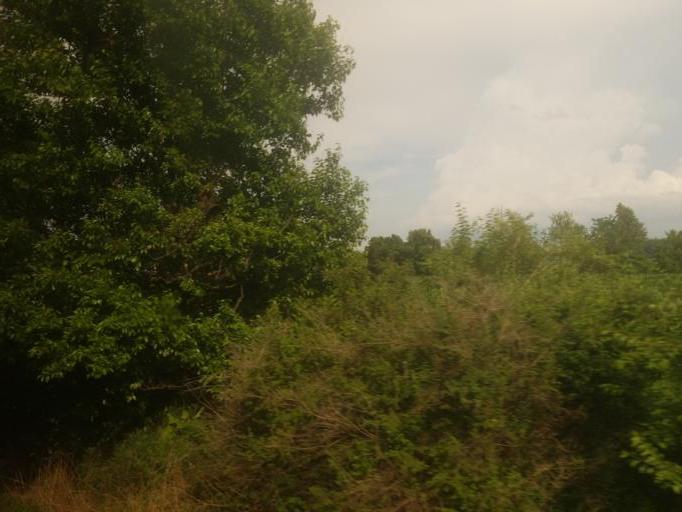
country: US
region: Illinois
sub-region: Henry County
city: Galva
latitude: 41.1093
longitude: -90.1684
